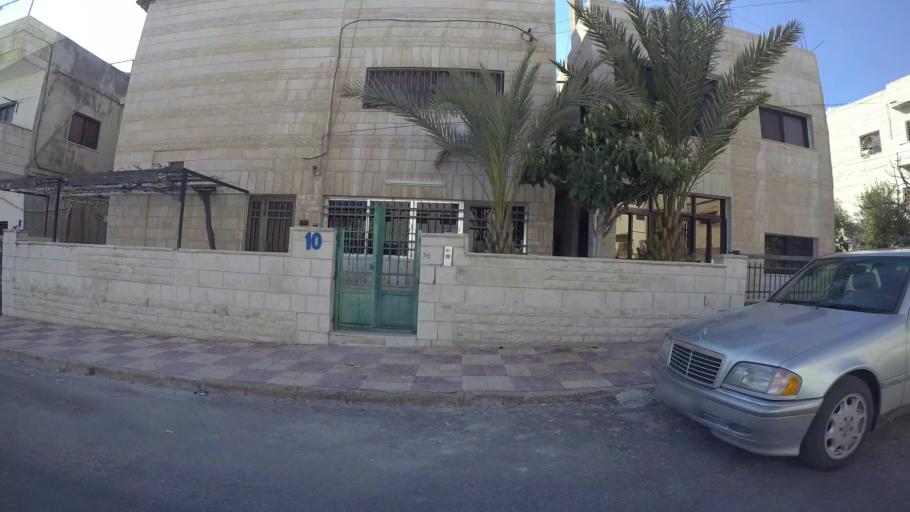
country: JO
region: Amman
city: Al Bunayyat ash Shamaliyah
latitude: 31.9056
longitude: 35.9141
